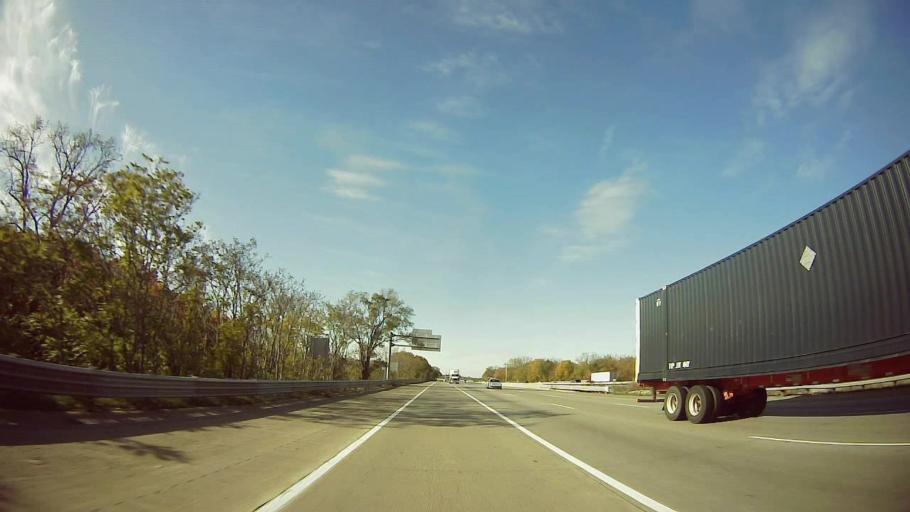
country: US
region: Michigan
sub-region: Wayne County
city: Romulus
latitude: 42.2260
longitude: -83.3938
